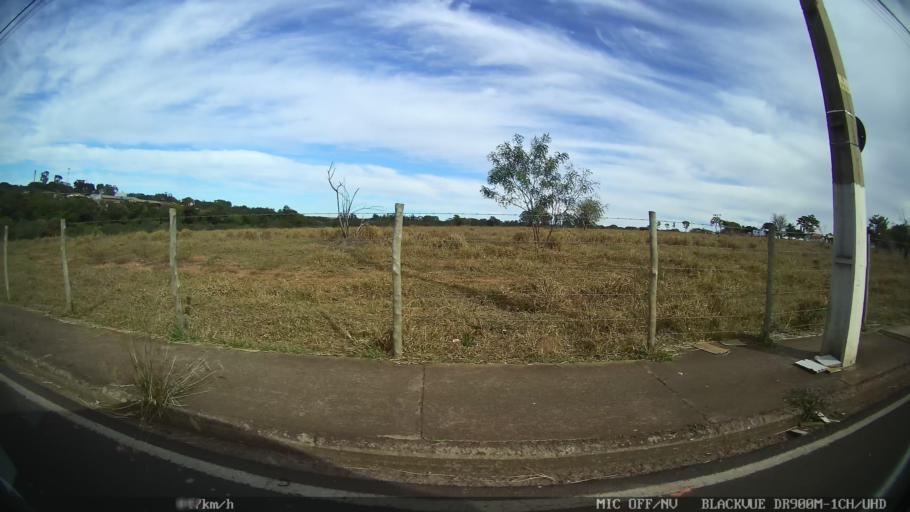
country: BR
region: Sao Paulo
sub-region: Catanduva
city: Catanduva
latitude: -21.1350
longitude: -48.9933
